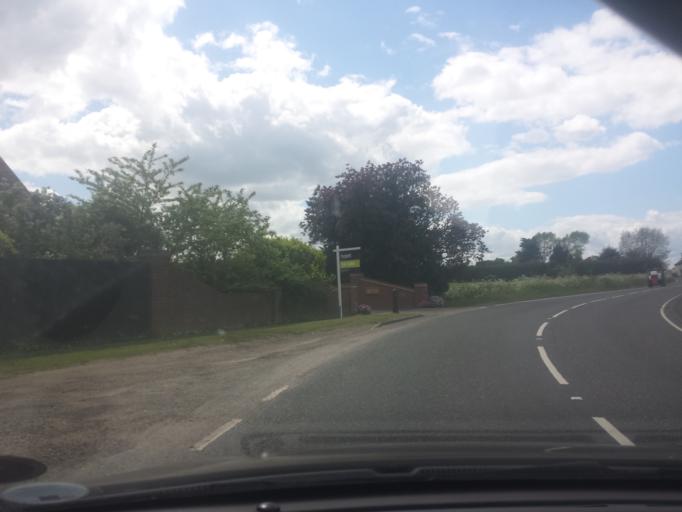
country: GB
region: England
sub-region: Essex
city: Little Clacton
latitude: 51.8433
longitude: 1.1601
